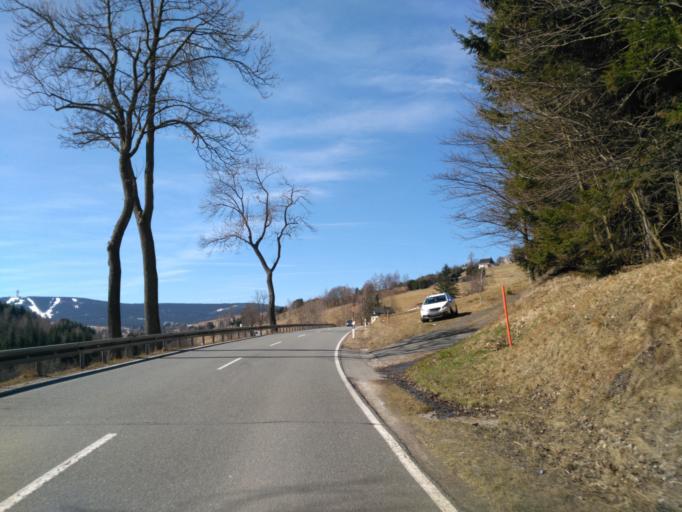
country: DE
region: Saxony
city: Kurort Oberwiesenthal
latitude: 50.4368
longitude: 12.9998
